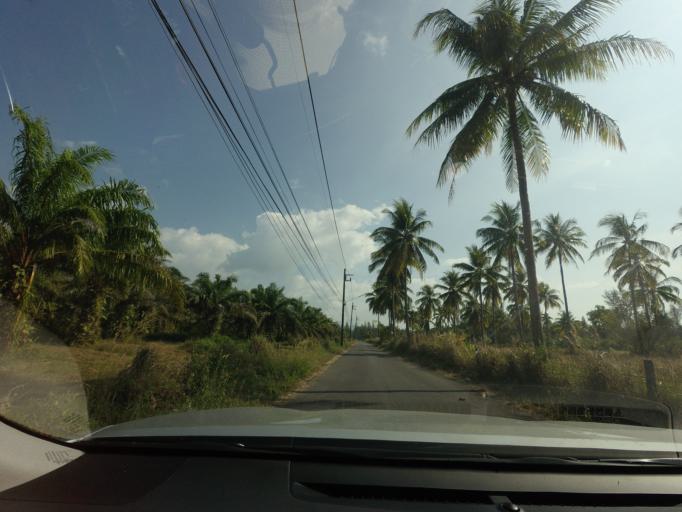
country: TH
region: Phangnga
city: Ban Khao Lak
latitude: 8.7262
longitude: 98.2430
